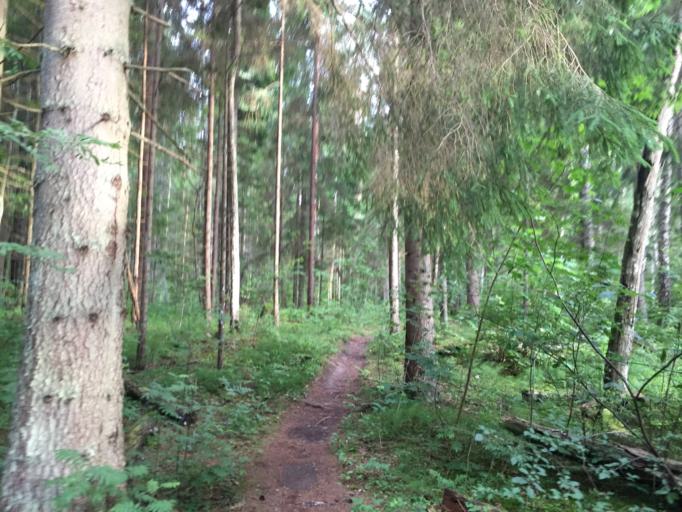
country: LV
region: Ligatne
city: Ligatne
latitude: 57.2323
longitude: 25.1526
